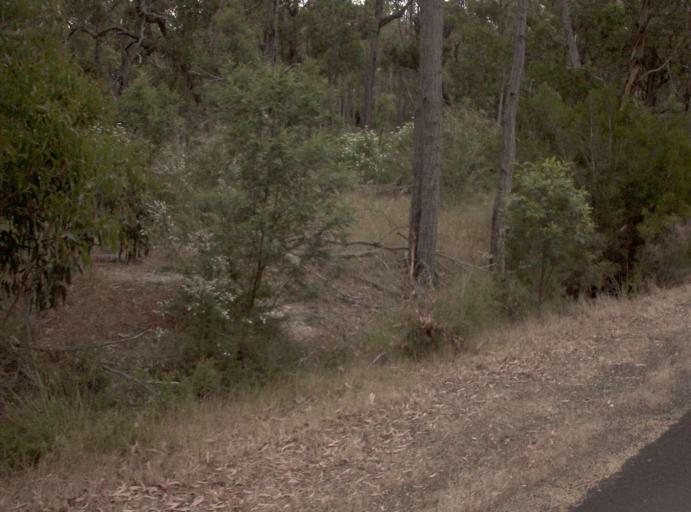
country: AU
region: Victoria
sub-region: Wellington
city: Sale
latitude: -38.4056
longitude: 146.9666
